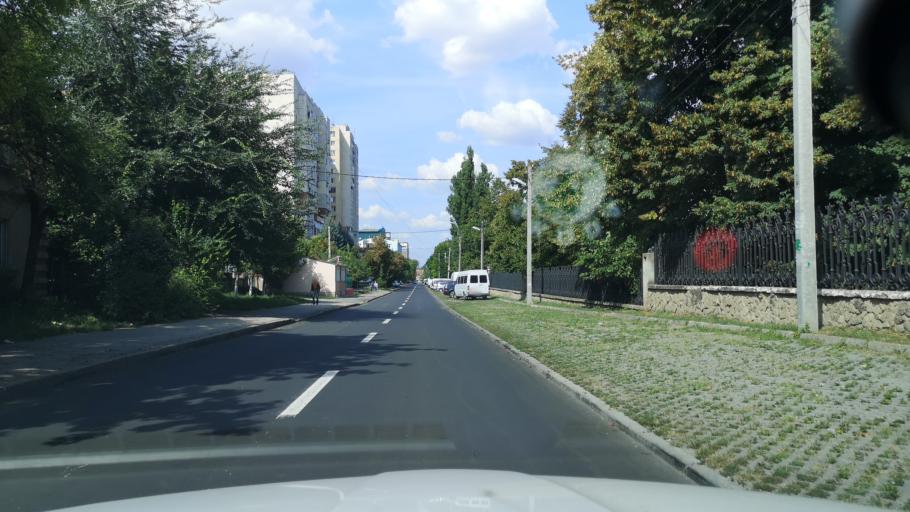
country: MD
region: Chisinau
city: Chisinau
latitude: 47.0260
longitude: 28.8087
